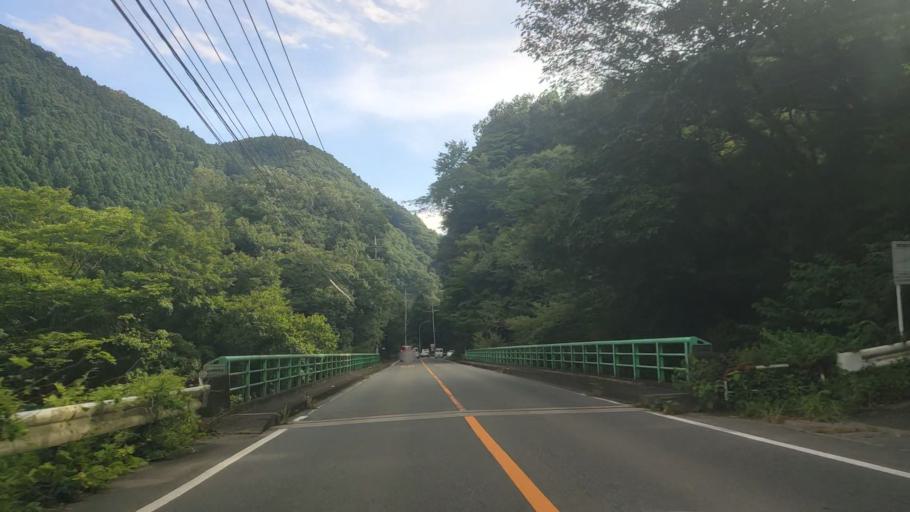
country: JP
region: Gunma
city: Omamacho-omama
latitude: 36.4850
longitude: 139.2632
